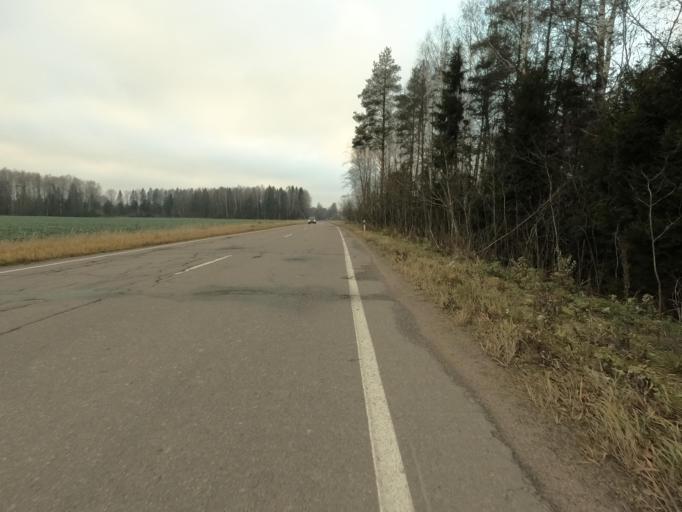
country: RU
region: Leningrad
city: Kirovsk
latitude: 59.8007
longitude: 30.9978
